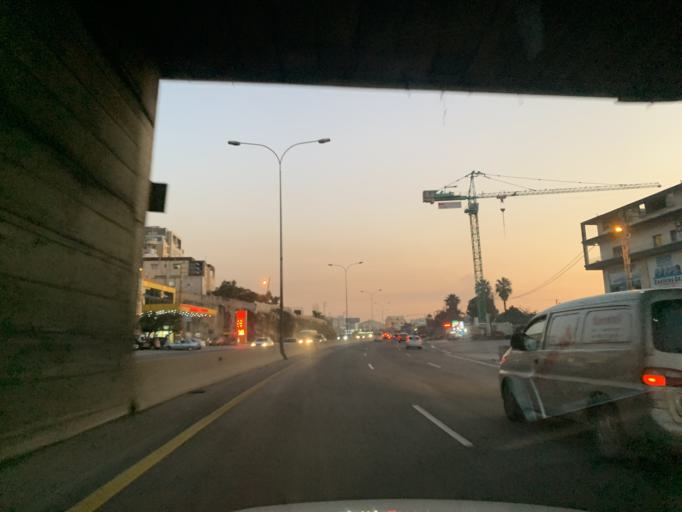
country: LB
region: Mont-Liban
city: Djounie
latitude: 34.0299
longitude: 35.6316
